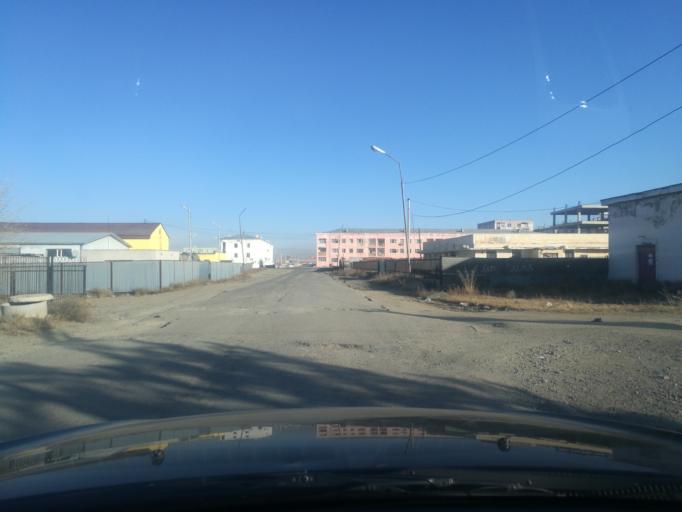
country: MN
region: Ulaanbaatar
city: Ulaanbaatar
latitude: 47.8546
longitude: 106.7575
